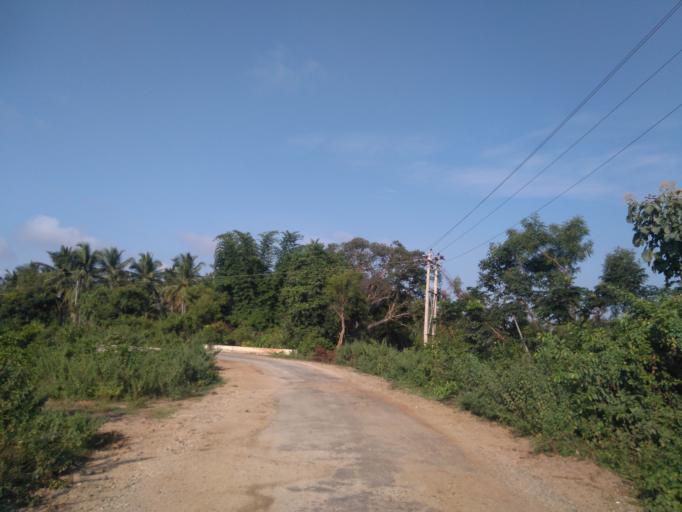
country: IN
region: Karnataka
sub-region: Mandya
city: Malavalli
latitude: 12.2812
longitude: 77.0677
